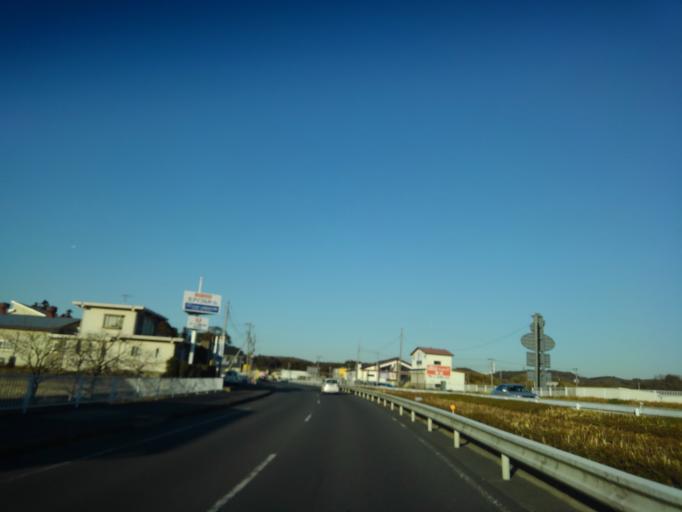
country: JP
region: Chiba
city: Kimitsu
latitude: 35.3129
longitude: 139.9262
